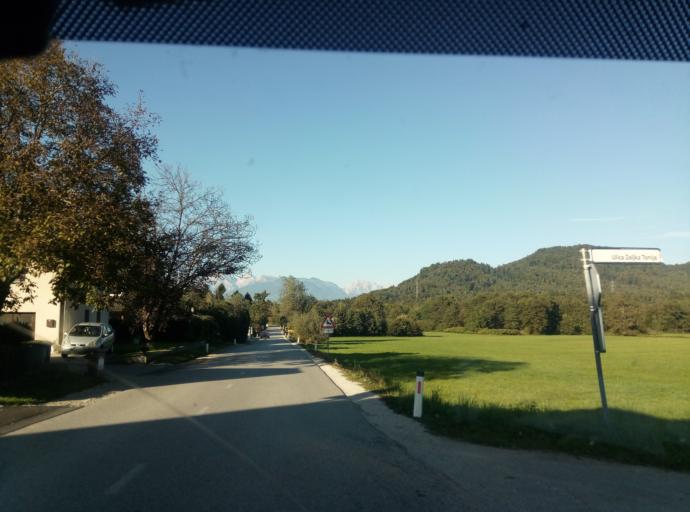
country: SI
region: Medvode
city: Zgornje Pirnice
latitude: 46.1283
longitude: 14.4767
